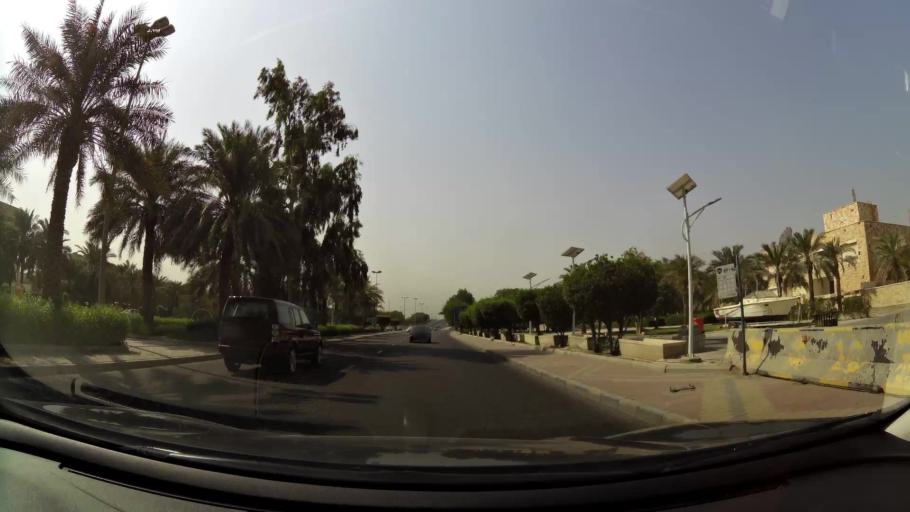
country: KW
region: Al Asimah
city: Ad Dasmah
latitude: 29.3368
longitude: 47.9925
